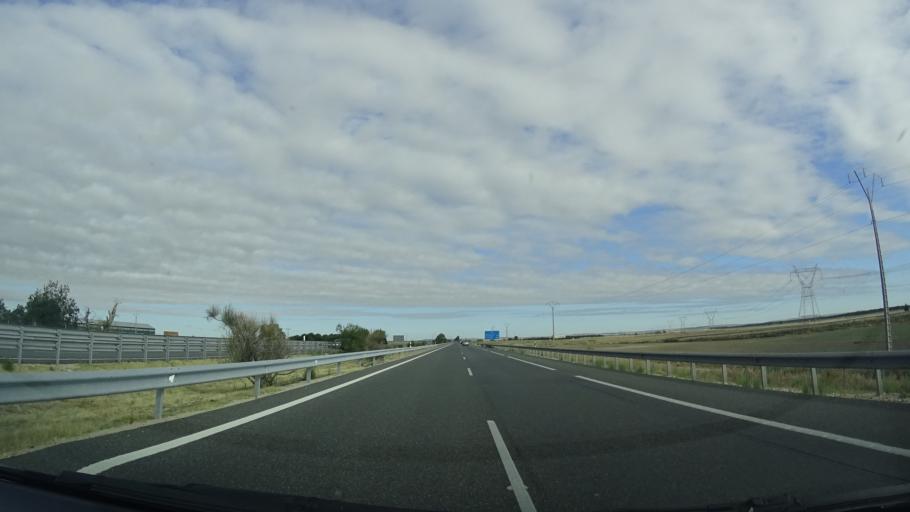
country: ES
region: Castille and Leon
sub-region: Provincia de Valladolid
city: San Vicente del Palacio
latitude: 41.2396
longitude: -4.8617
